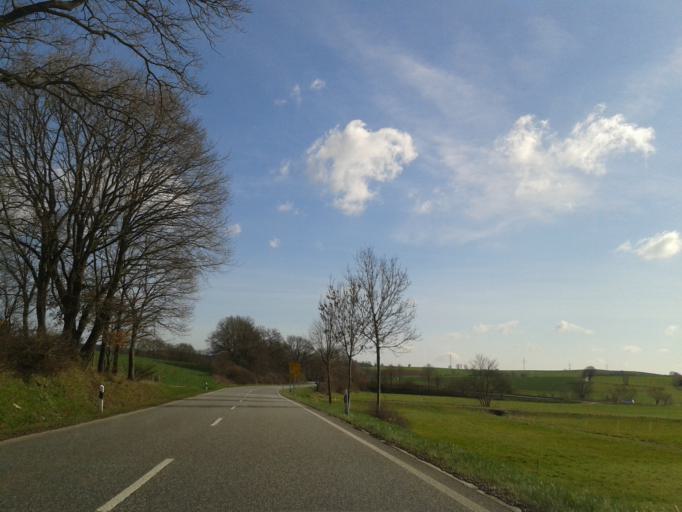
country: DE
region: Hesse
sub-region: Regierungsbezirk Giessen
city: Munchhausen
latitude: 50.9743
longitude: 8.6993
